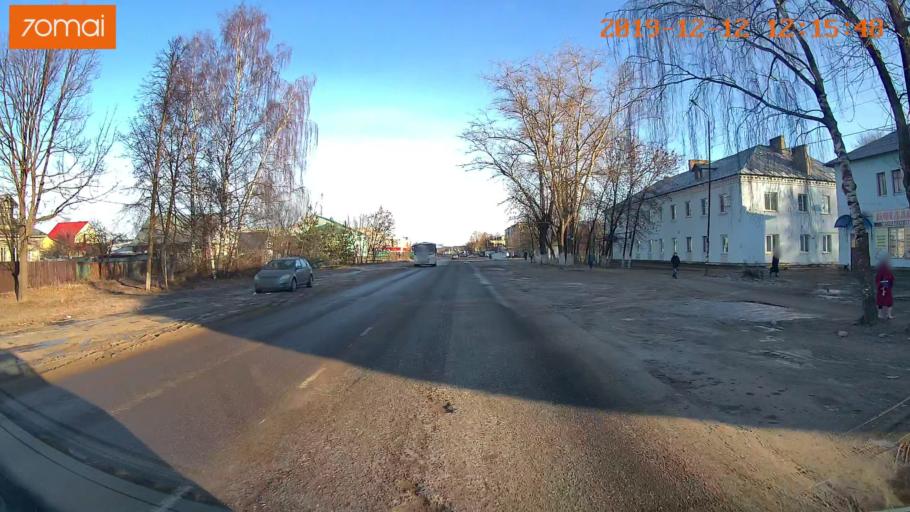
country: RU
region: Ivanovo
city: Kokhma
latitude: 56.9380
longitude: 41.1025
